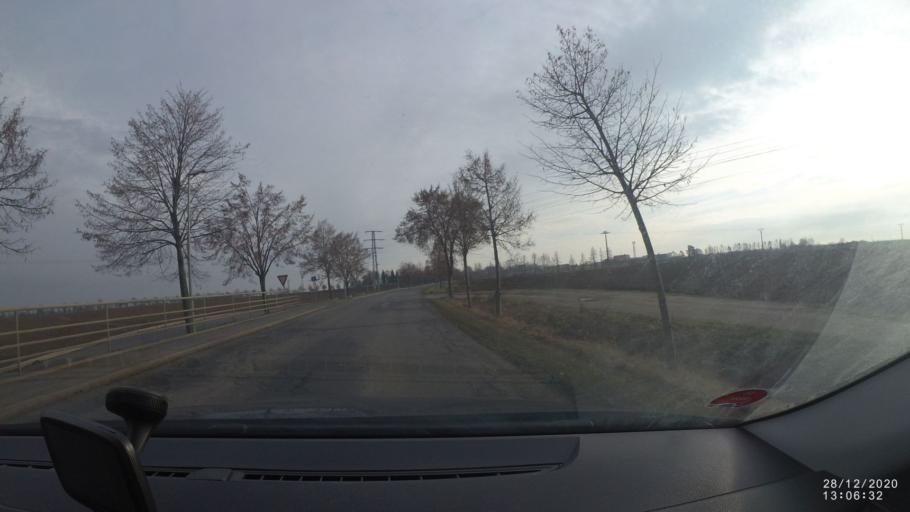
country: CZ
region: Central Bohemia
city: Zelenec
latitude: 50.1428
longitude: 14.6539
